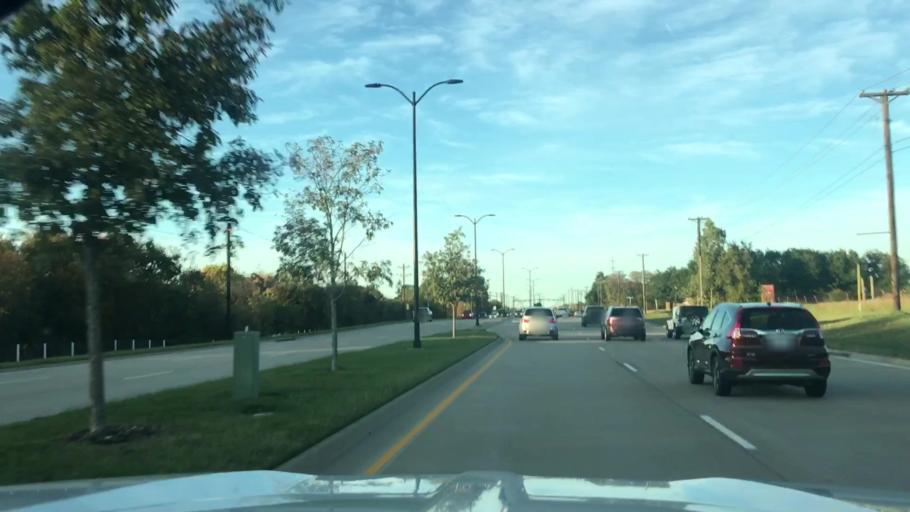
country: US
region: Texas
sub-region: Collin County
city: Frisco
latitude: 33.1839
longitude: -96.8029
